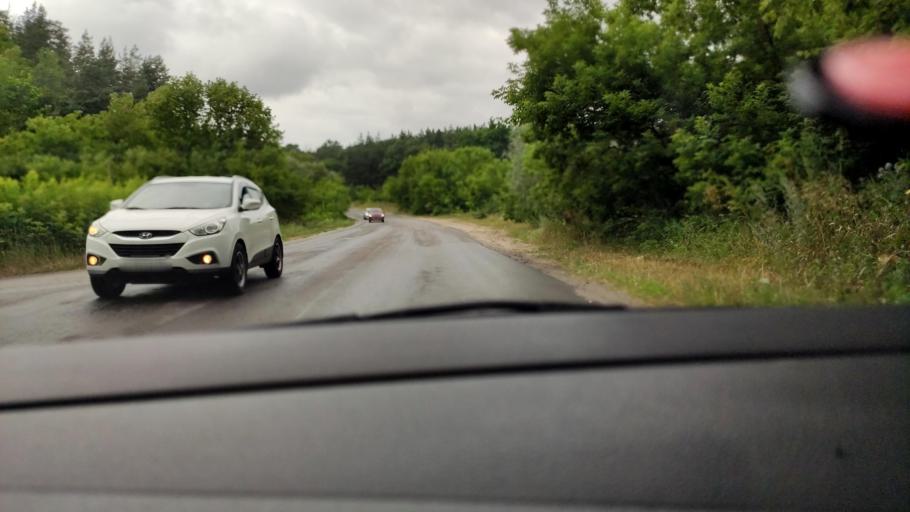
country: RU
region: Voronezj
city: Ramon'
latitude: 51.9030
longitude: 39.3415
